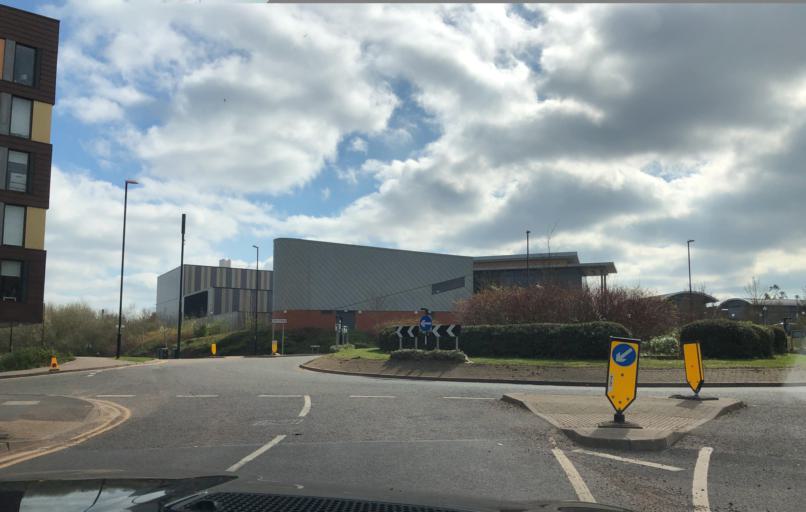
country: GB
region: England
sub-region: Coventry
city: Coventry
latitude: 52.4033
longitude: -1.5031
